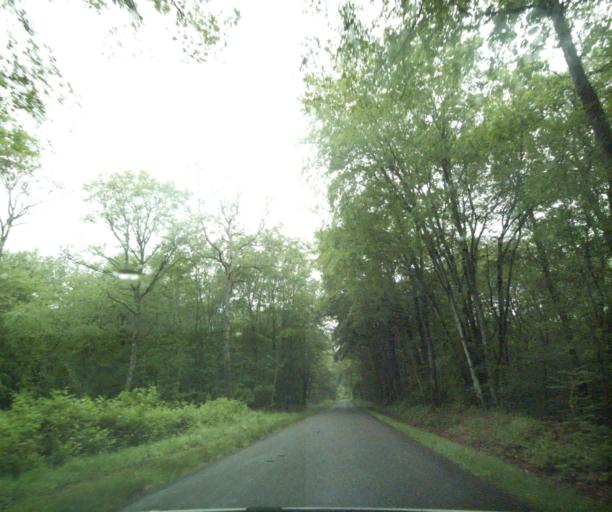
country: FR
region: Bourgogne
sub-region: Departement de Saone-et-Loire
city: Paray-le-Monial
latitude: 46.4250
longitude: 4.1869
